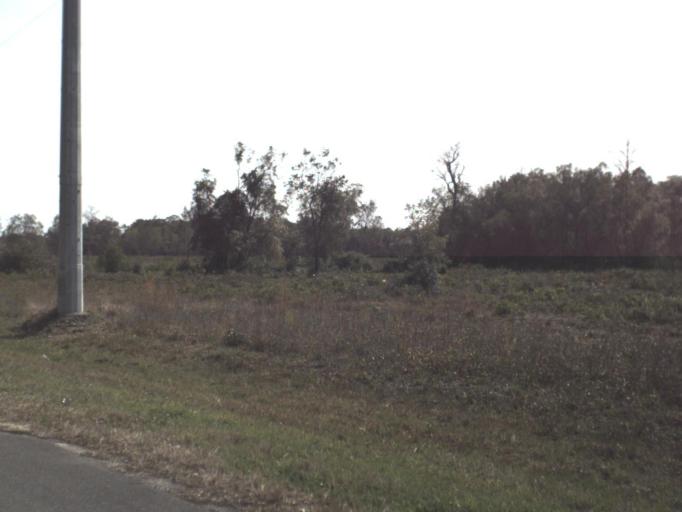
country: US
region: Florida
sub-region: Franklin County
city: Carrabelle
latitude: 29.9485
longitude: -84.5028
